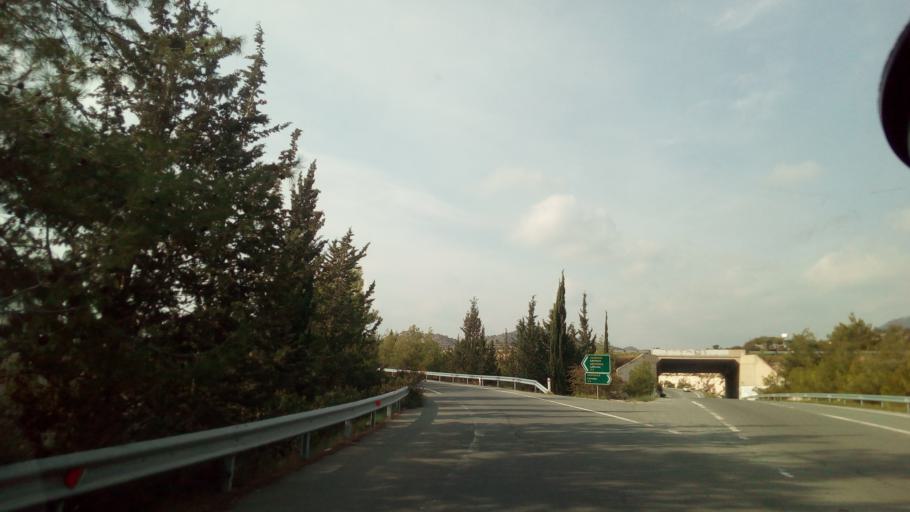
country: CY
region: Larnaka
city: Kofinou
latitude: 34.8524
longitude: 33.4498
